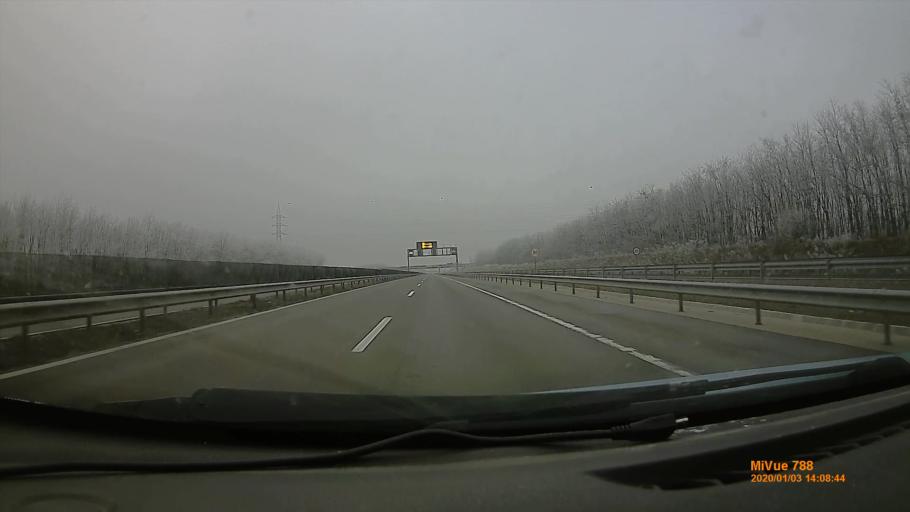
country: HU
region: Pest
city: Nagytarcsa
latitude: 47.5079
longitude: 19.2907
